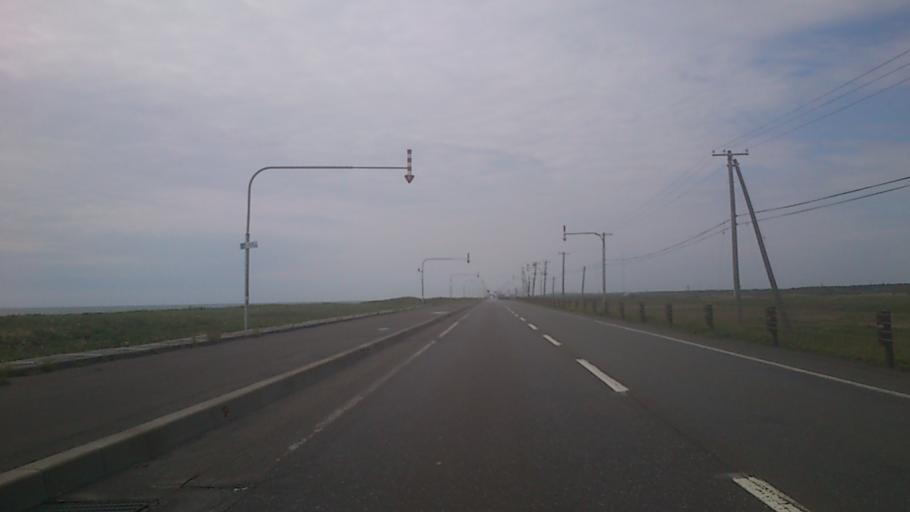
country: JP
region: Hokkaido
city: Makubetsu
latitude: 44.9856
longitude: 141.6907
